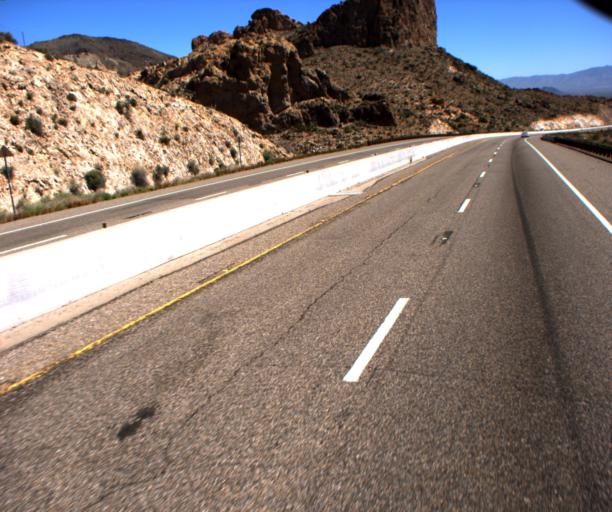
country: US
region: Arizona
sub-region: Mohave County
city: Golden Valley
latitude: 35.2212
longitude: -114.3880
